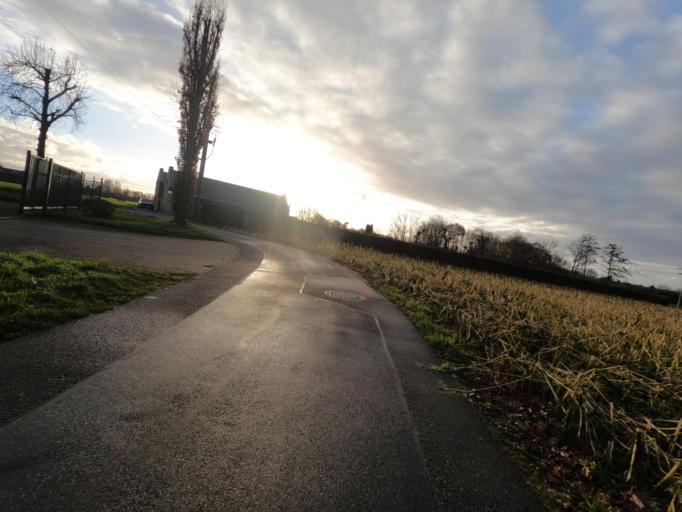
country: DE
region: North Rhine-Westphalia
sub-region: Regierungsbezirk Koln
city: Heinsberg
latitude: 51.0865
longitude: 6.0792
